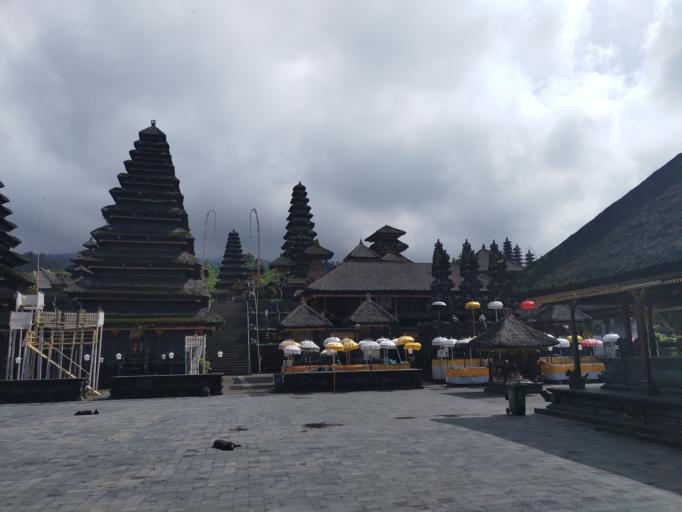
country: ID
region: Bali
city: Banjar Geriana Kangin
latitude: -8.3740
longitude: 115.4522
